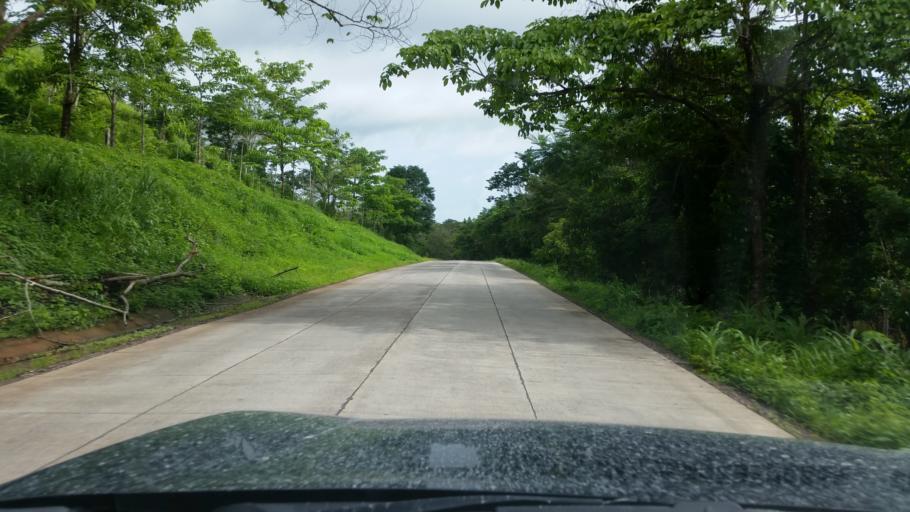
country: NI
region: Atlantico Norte (RAAN)
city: Siuna
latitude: 13.5408
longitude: -84.8241
